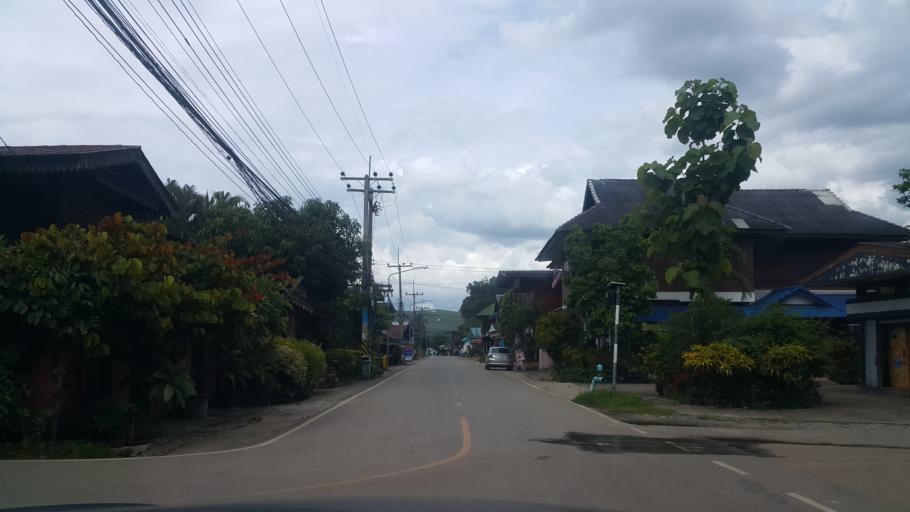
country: TH
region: Chiang Mai
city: Mae Taeng
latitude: 19.1818
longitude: 98.9905
